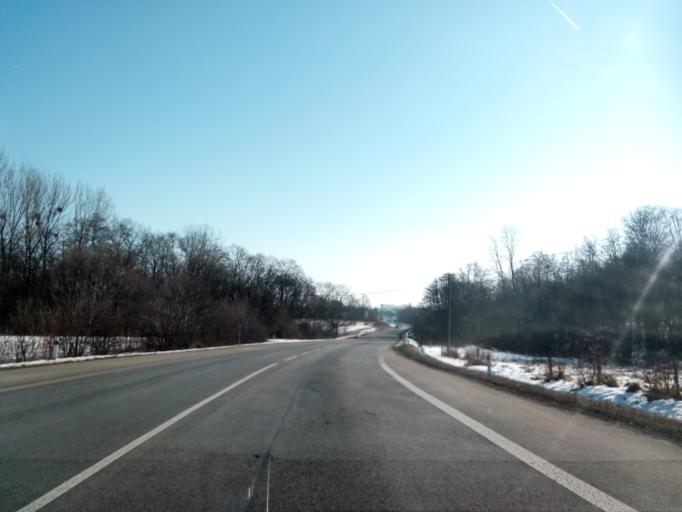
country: SK
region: Kosicky
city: Secovce
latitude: 48.7357
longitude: 21.5693
